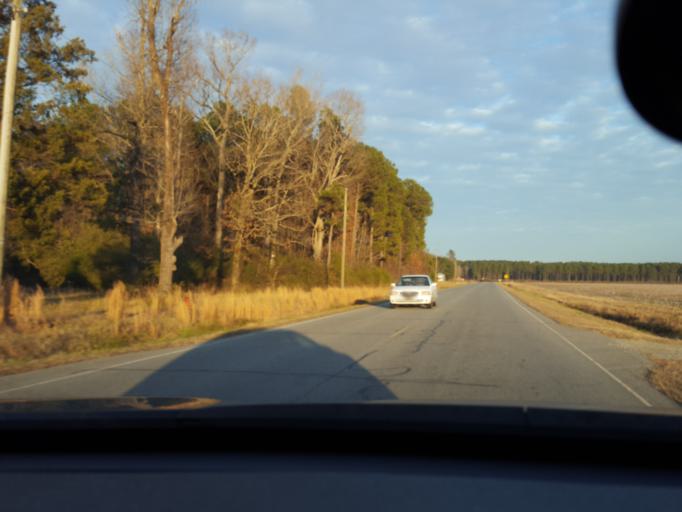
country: US
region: North Carolina
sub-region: Hertford County
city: Murfreesboro
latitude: 36.2757
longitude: -77.2130
